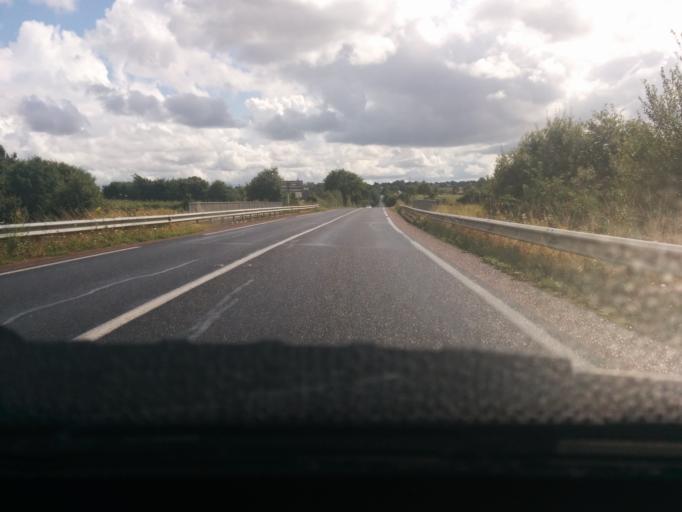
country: FR
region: Pays de la Loire
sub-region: Departement de la Vendee
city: Chambretaud
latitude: 46.9285
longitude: -0.9897
